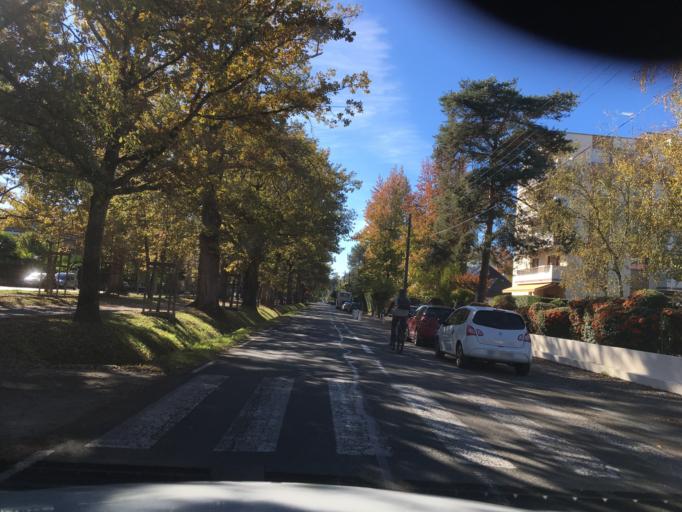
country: FR
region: Aquitaine
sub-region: Departement des Pyrenees-Atlantiques
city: Bizanos
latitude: 43.3071
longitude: -0.3417
